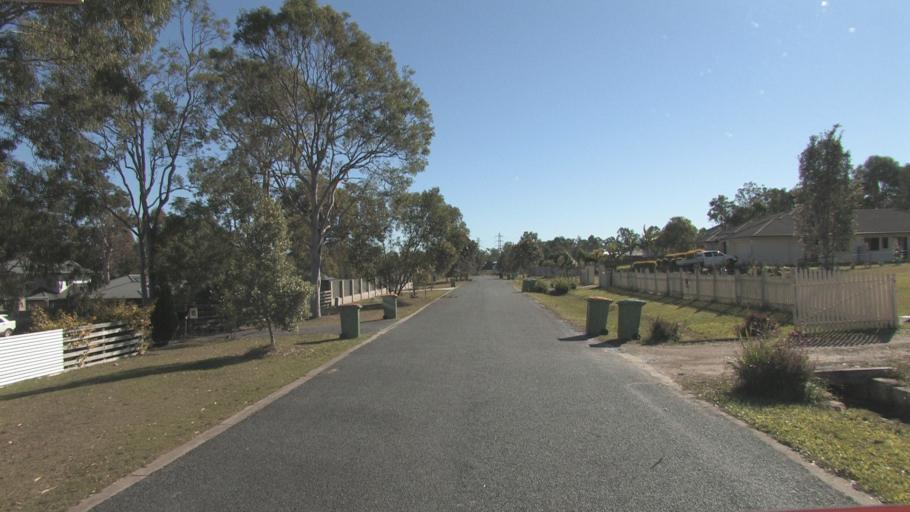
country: AU
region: Queensland
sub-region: Logan
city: North Maclean
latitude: -27.7394
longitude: 152.9557
